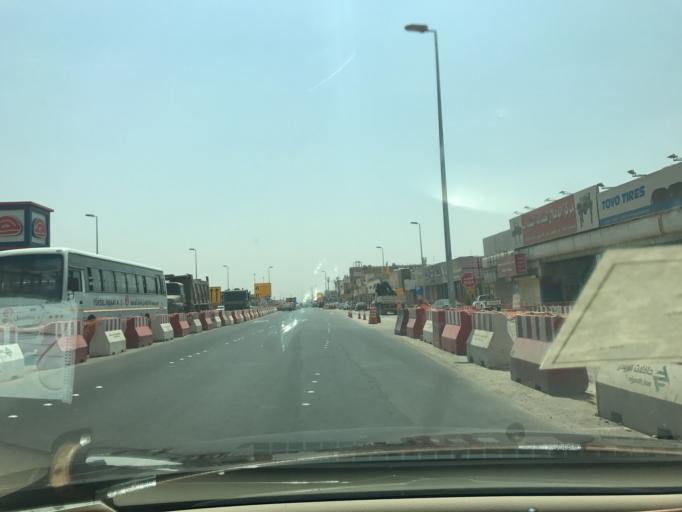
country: SA
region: Ar Riyad
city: Riyadh
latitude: 24.7501
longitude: 46.7722
